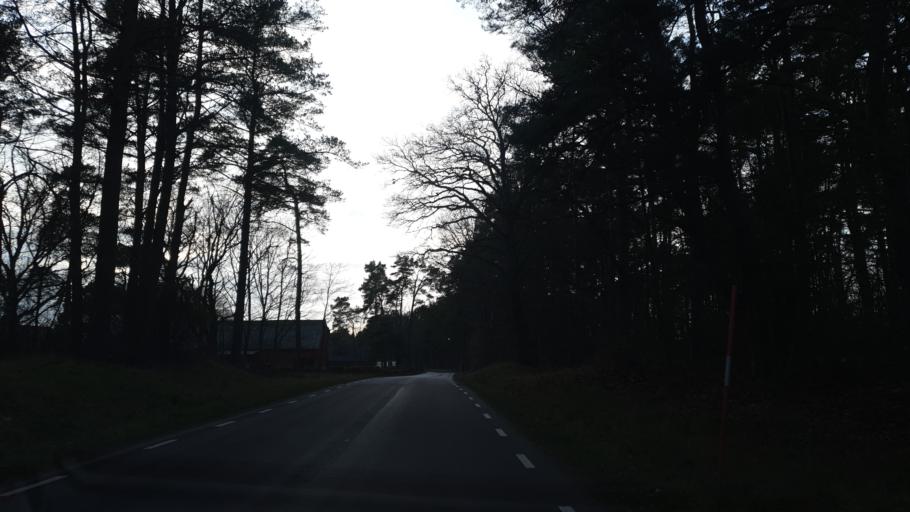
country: SE
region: Blekinge
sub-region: Karlskrona Kommun
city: Jaemjoe
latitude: 56.2053
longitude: 15.9622
